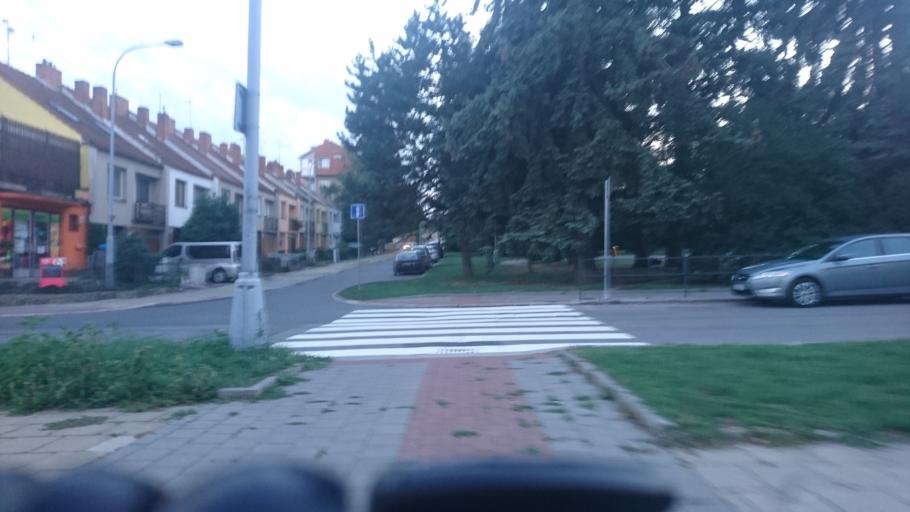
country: CZ
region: South Moravian
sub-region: Mesto Brno
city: Mokra Hora
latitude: 49.2426
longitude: 16.5858
